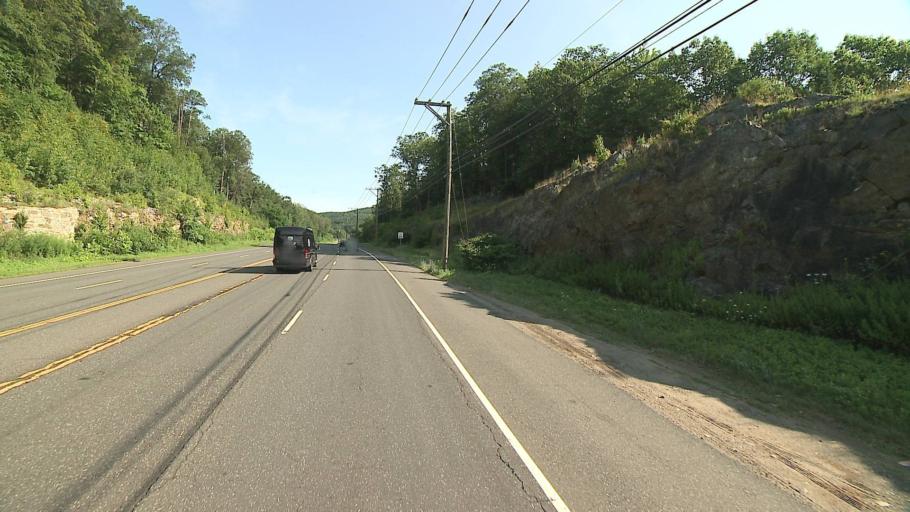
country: US
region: Connecticut
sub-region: Fairfield County
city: Danbury
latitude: 41.3394
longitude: -73.4697
